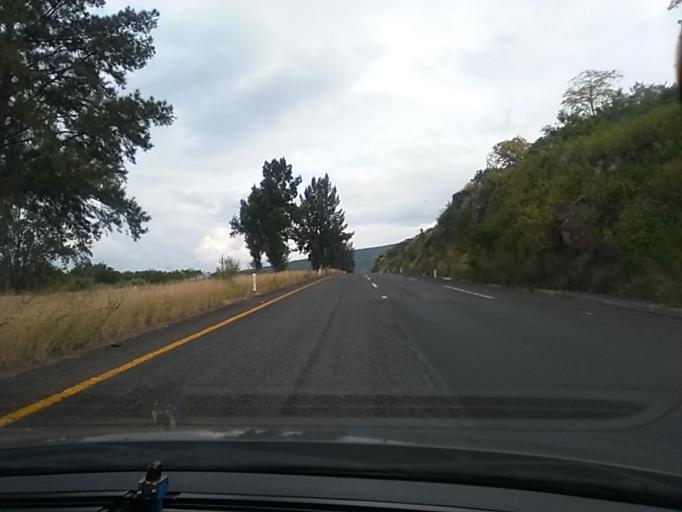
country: MX
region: Michoacan
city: Ixtlan
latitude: 20.2222
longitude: -102.3678
